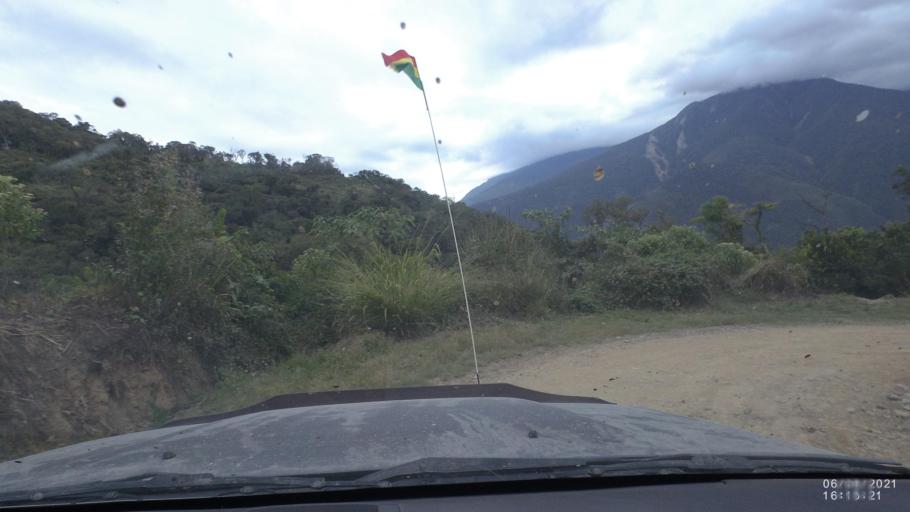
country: BO
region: La Paz
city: Quime
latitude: -16.5521
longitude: -66.7375
